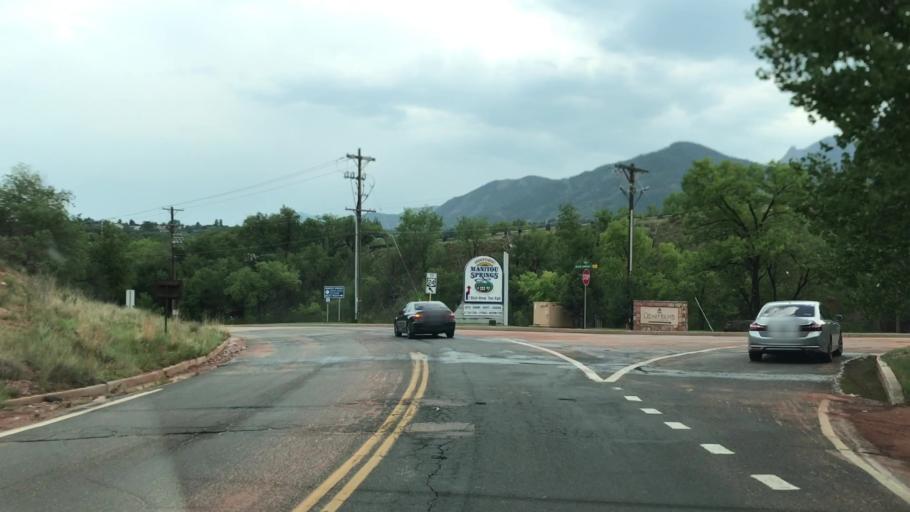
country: US
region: Colorado
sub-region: El Paso County
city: Manitou Springs
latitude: 38.8604
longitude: -104.8979
